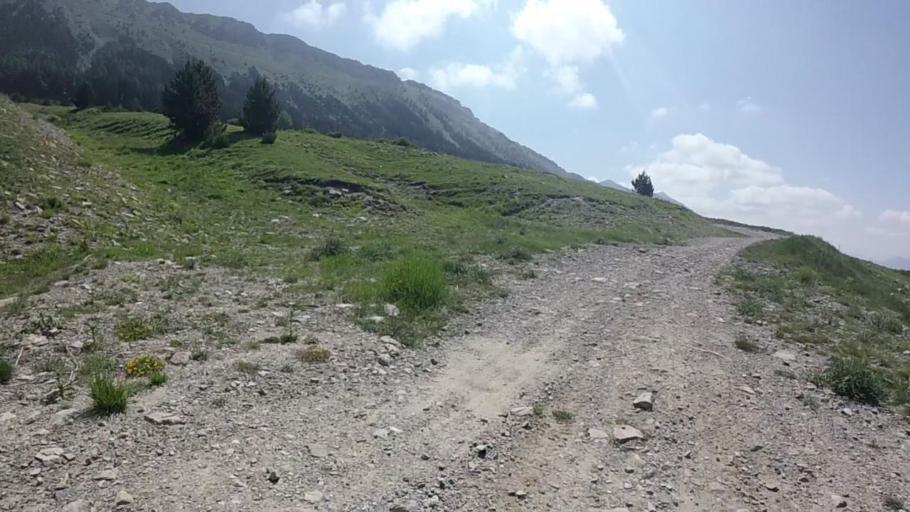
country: FR
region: Provence-Alpes-Cote d'Azur
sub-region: Departement des Alpes-de-Haute-Provence
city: Seyne-les-Alpes
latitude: 44.3996
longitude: 6.3735
